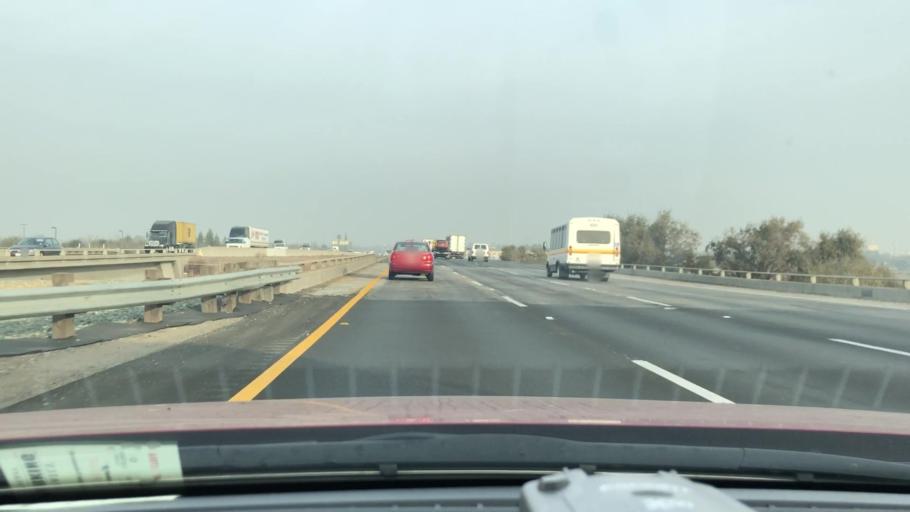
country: US
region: California
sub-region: San Joaquin County
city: French Camp
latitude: 37.8855
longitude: -121.2795
